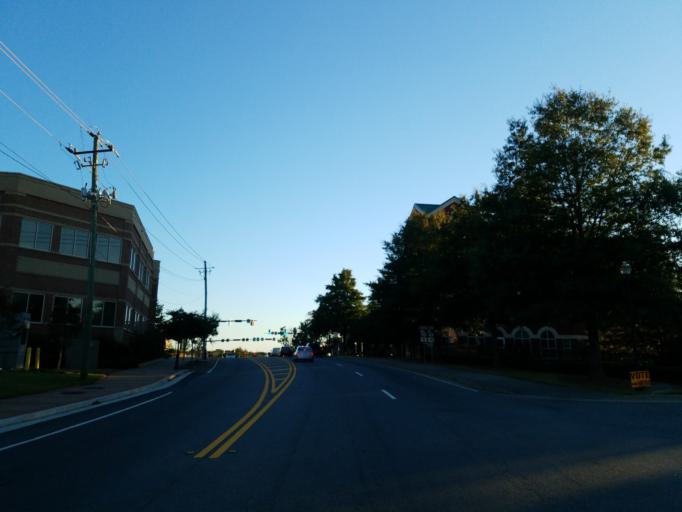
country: US
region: Georgia
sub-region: Forsyth County
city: Cumming
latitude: 34.2080
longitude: -84.1390
